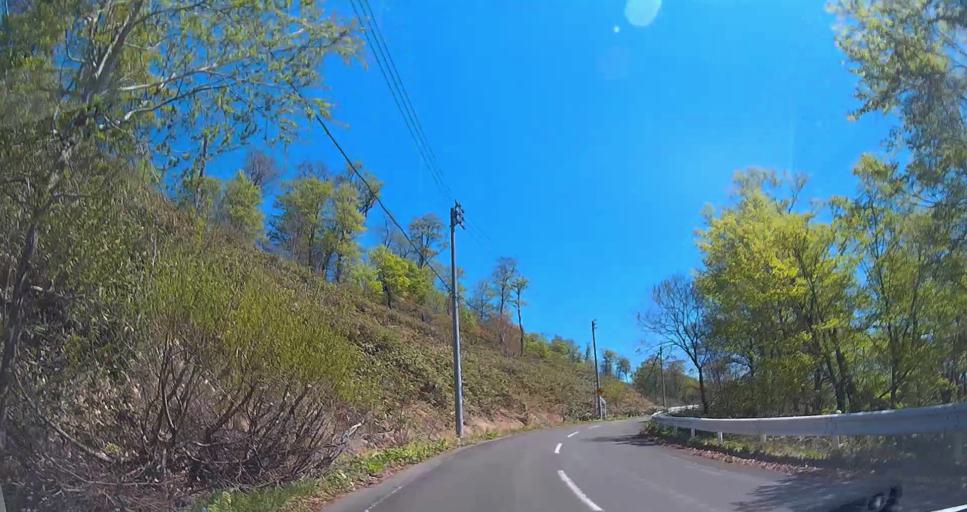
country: JP
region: Aomori
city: Mutsu
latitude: 41.2306
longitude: 140.8119
